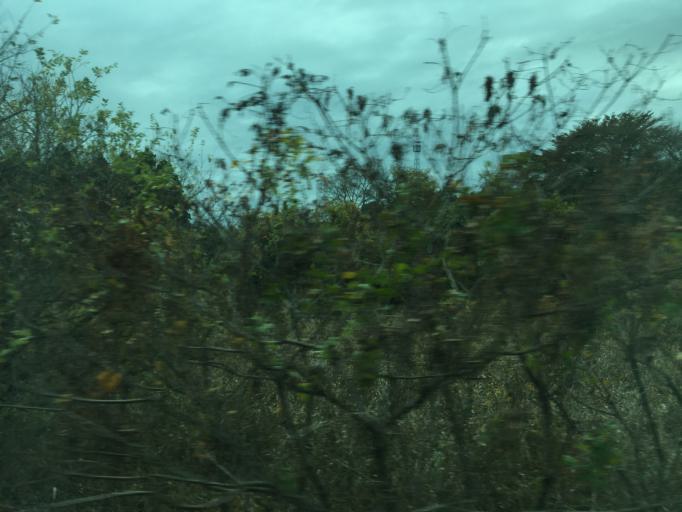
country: JP
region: Ibaraki
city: Tomobe
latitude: 36.3486
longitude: 140.2822
